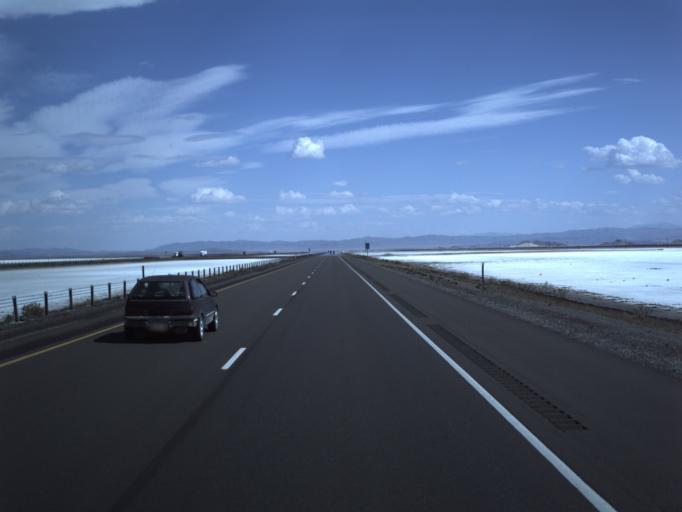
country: US
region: Utah
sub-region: Tooele County
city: Wendover
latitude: 40.7288
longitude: -113.4099
